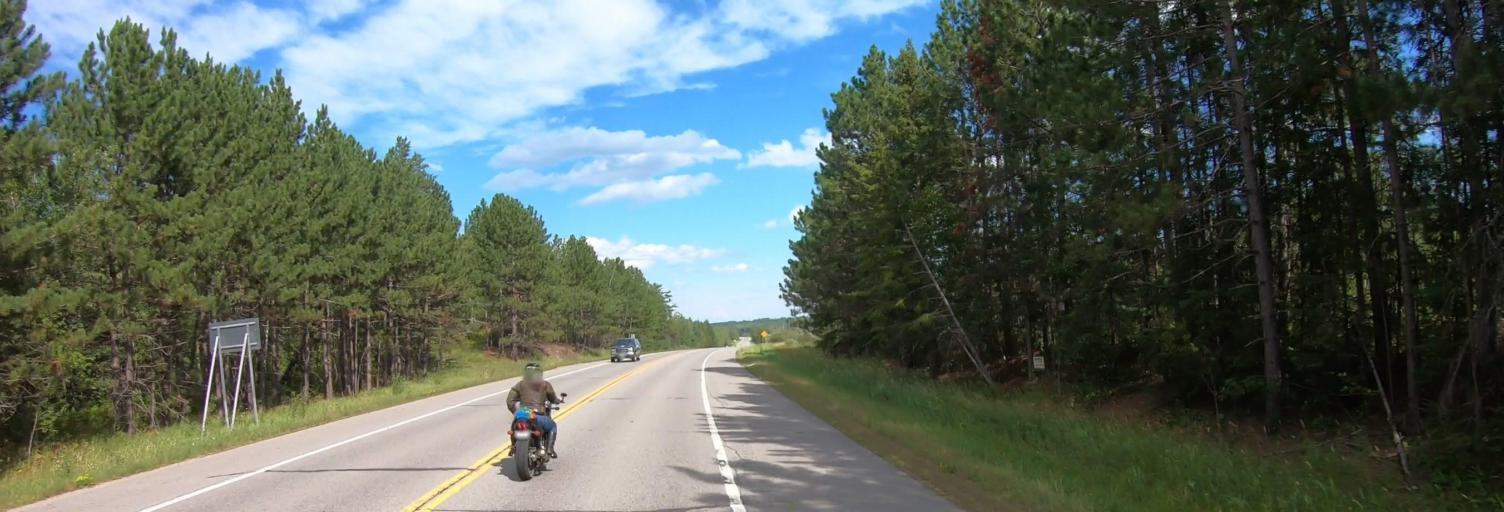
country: US
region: Minnesota
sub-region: Saint Louis County
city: Aurora
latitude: 47.7975
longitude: -92.3297
